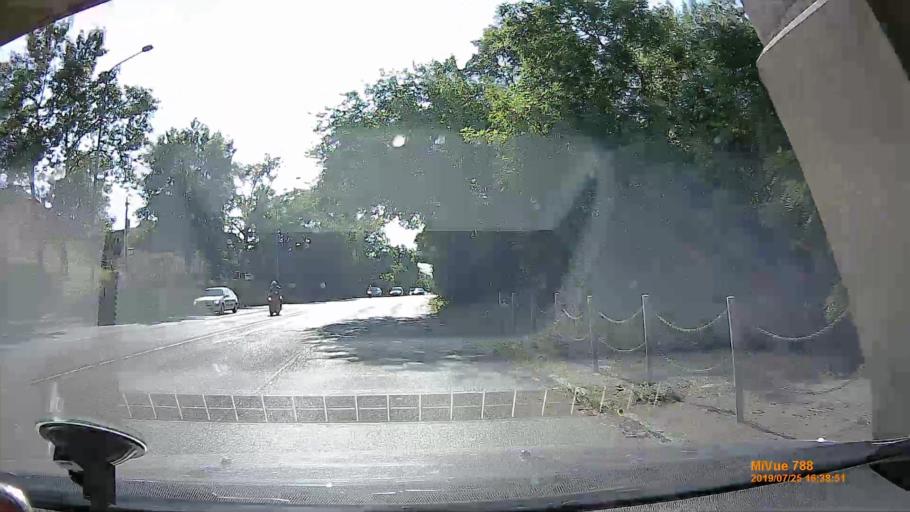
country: HU
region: Heves
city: Gyongyos
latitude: 47.7747
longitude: 19.9360
